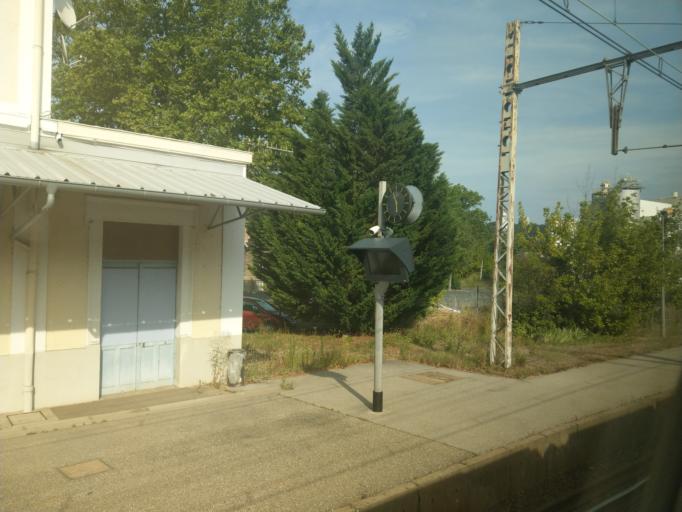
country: FR
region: Rhone-Alpes
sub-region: Departement du Rhone
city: Fontaines-sur-Saone
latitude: 45.8290
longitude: 4.8466
